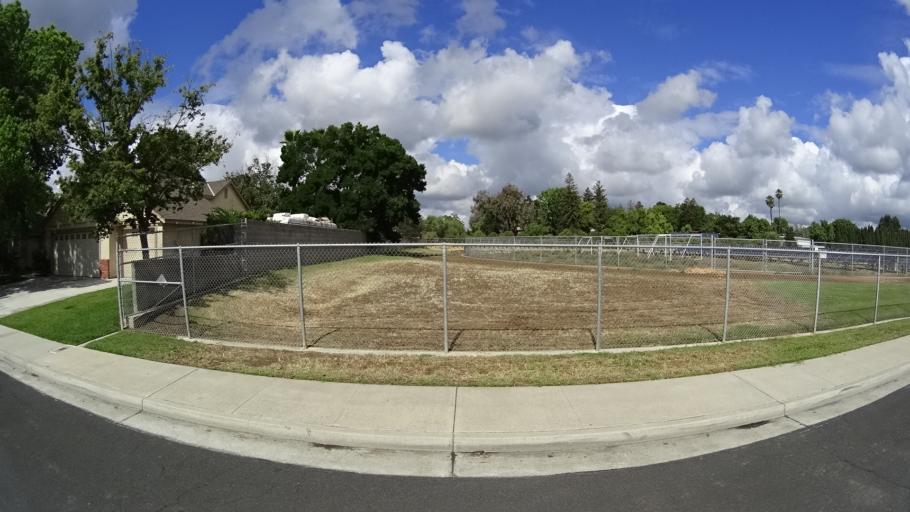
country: US
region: California
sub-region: Kings County
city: Lucerne
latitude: 36.3683
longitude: -119.6495
